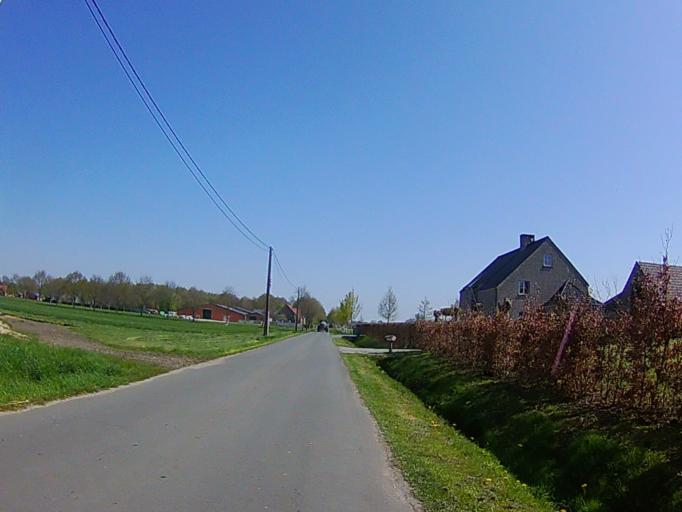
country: BE
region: Flanders
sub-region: Provincie Antwerpen
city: Brecht
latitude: 51.3289
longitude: 4.6259
